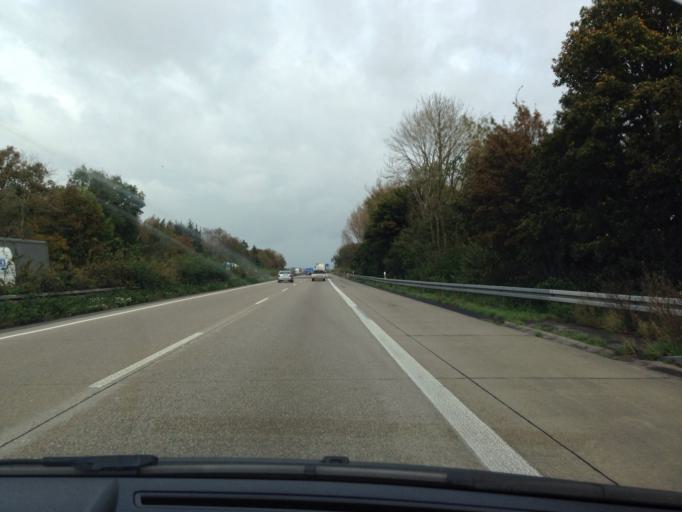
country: DE
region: North Rhine-Westphalia
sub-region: Regierungsbezirk Munster
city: Senden
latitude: 51.8688
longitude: 7.5761
